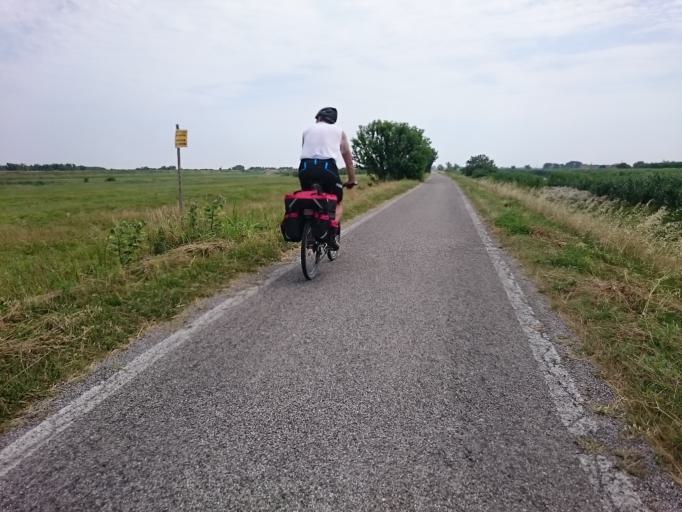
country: IT
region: Veneto
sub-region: Provincia di Venezia
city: Valli
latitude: 45.1890
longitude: 12.2197
